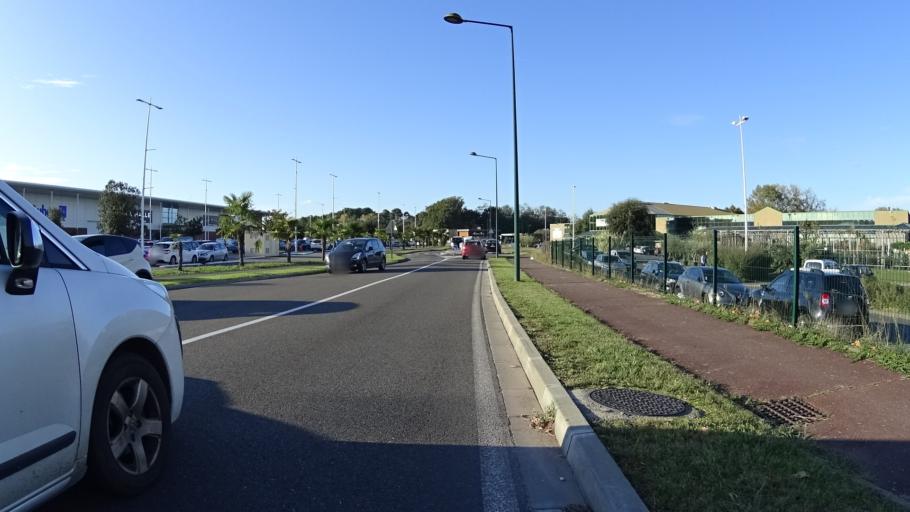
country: FR
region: Aquitaine
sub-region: Departement des Landes
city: Saint-Paul-les-Dax
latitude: 43.7301
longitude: -1.0383
